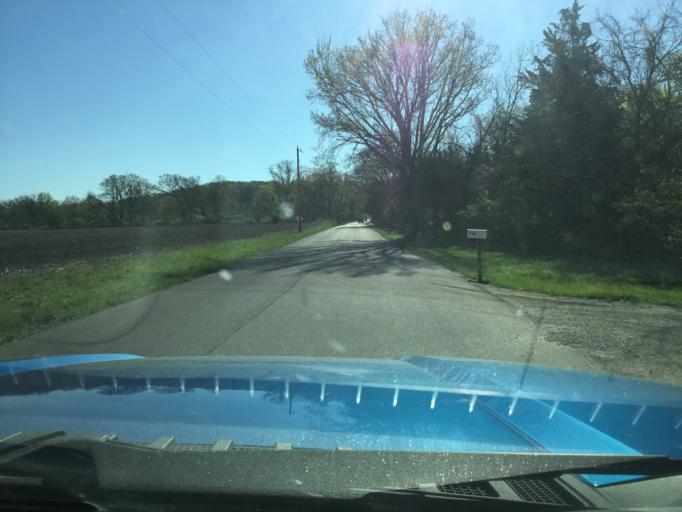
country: US
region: Kansas
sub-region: Douglas County
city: Lawrence
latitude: 38.9933
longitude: -95.3049
